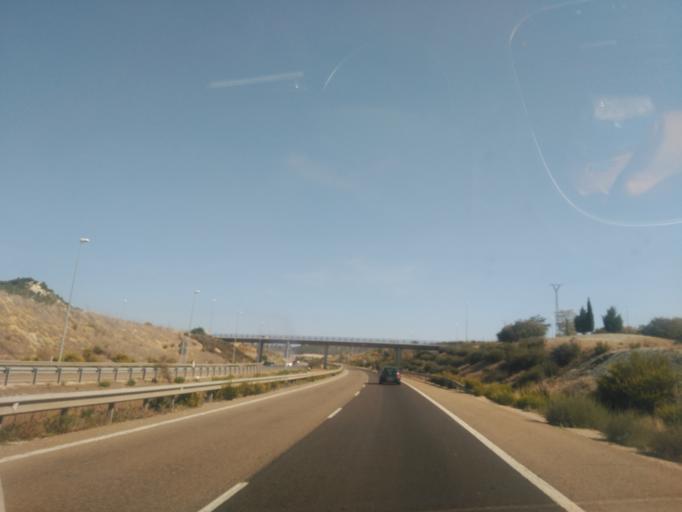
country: ES
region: Castille and Leon
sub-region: Provincia de Valladolid
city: Cisterniga
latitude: 41.6170
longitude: -4.6871
